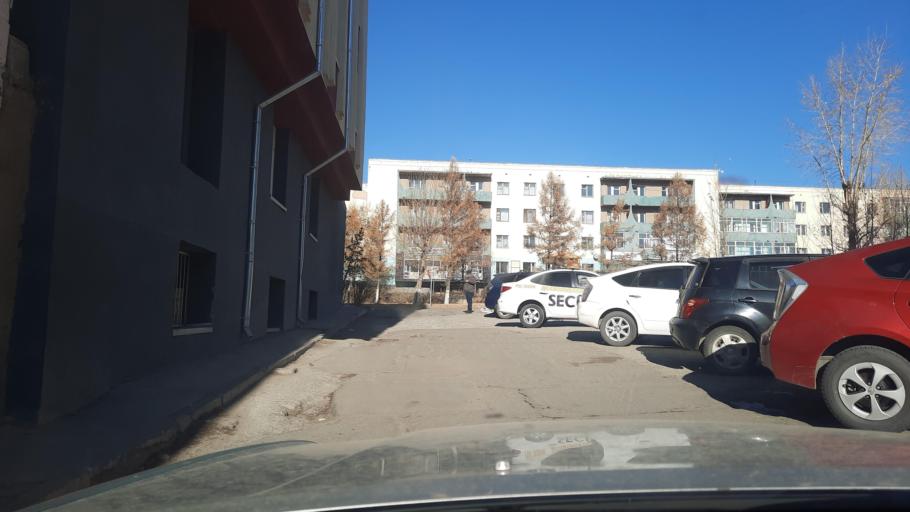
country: MN
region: Orhon
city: Erdenet
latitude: 49.0307
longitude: 104.0573
